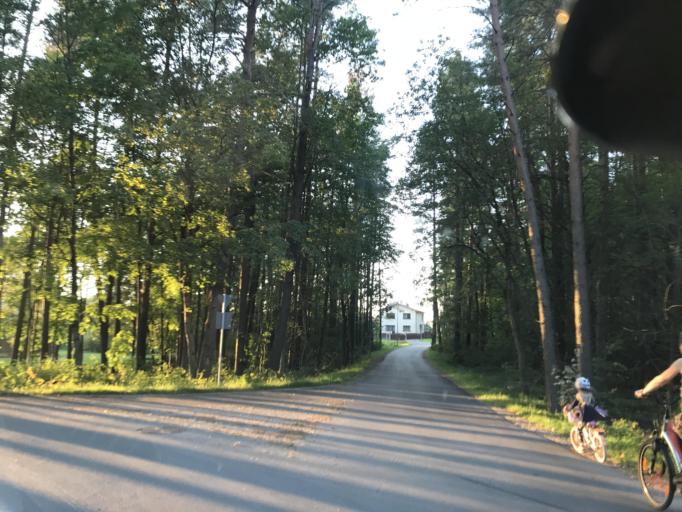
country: LV
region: Ikskile
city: Ikskile
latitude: 56.8260
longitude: 24.5082
